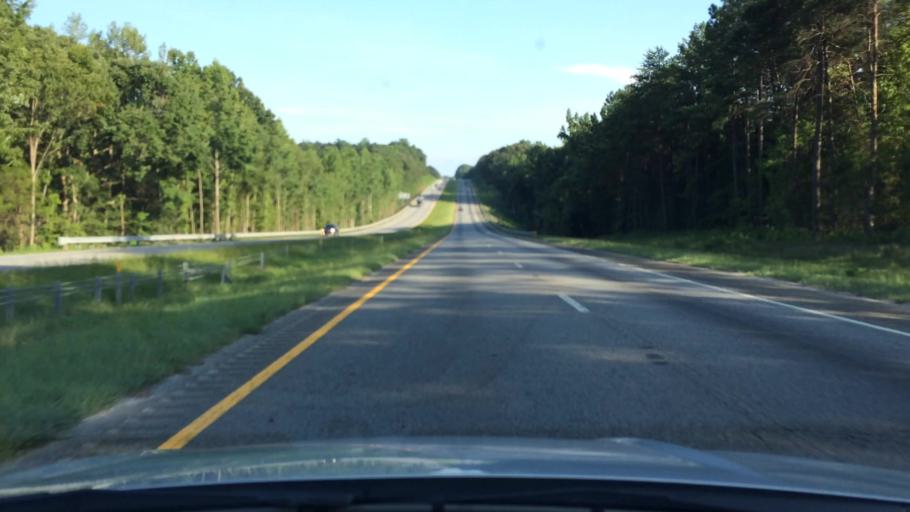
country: US
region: South Carolina
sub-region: Spartanburg County
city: Woodruff
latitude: 34.7346
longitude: -81.9529
